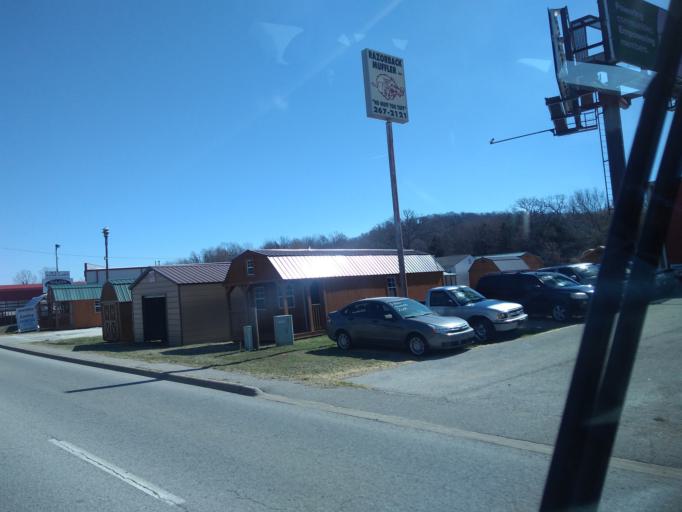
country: US
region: Arkansas
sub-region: Washington County
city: Farmington
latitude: 36.0454
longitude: -94.2297
